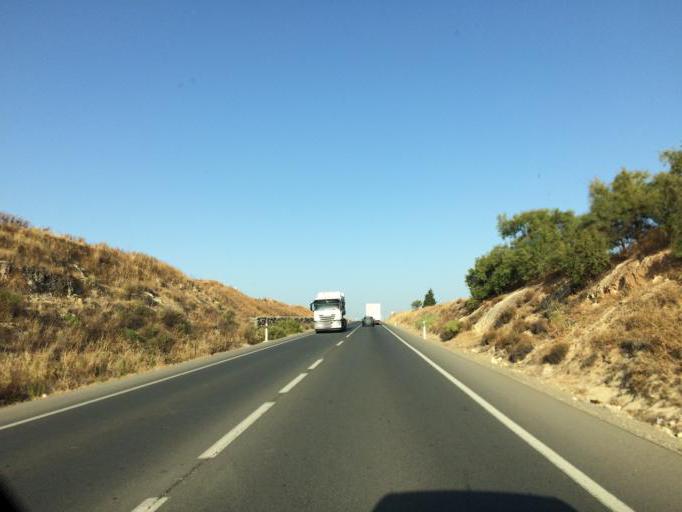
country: ES
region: Andalusia
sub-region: Provincia de Malaga
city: Campillos
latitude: 37.0513
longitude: -4.8120
